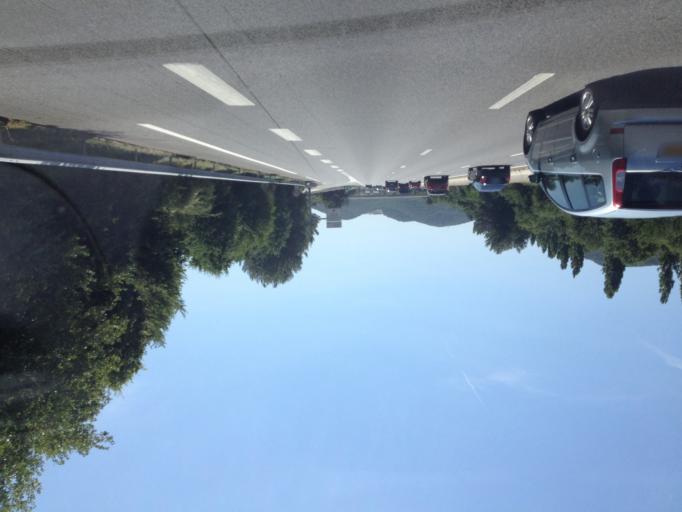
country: FR
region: Rhone-Alpes
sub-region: Departement de la Drome
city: Malataverne
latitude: 44.4848
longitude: 4.7668
